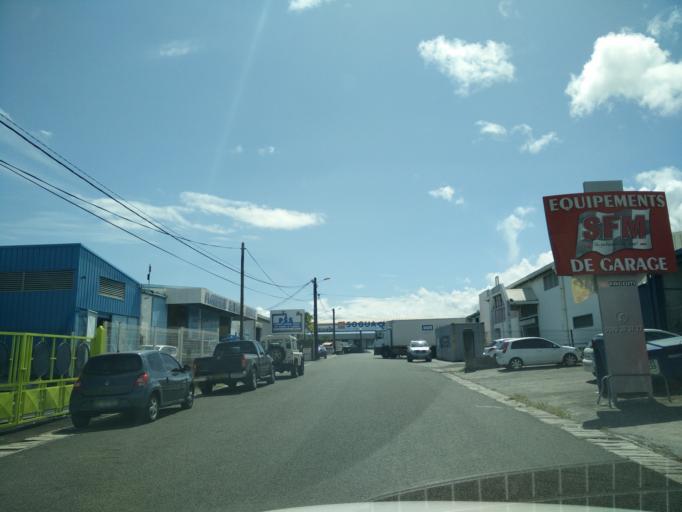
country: GP
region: Guadeloupe
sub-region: Guadeloupe
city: Pointe-a-Pitre
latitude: 16.2439
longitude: -61.5563
